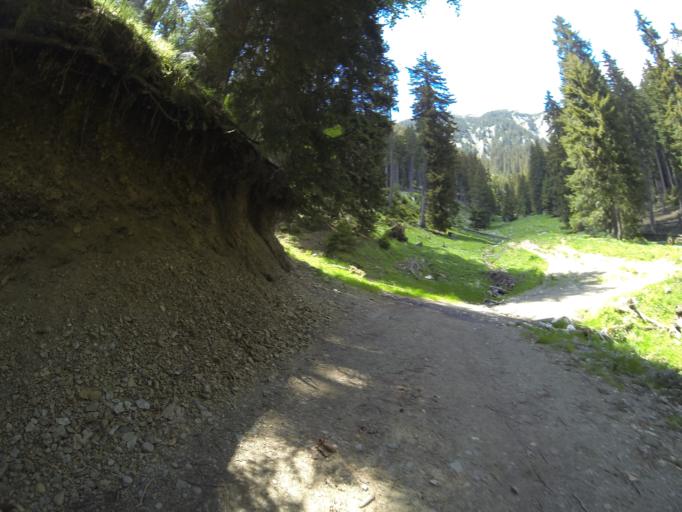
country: RO
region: Brasov
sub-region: Comuna Zarnesti
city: Zarnesti
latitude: 45.5465
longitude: 25.2500
